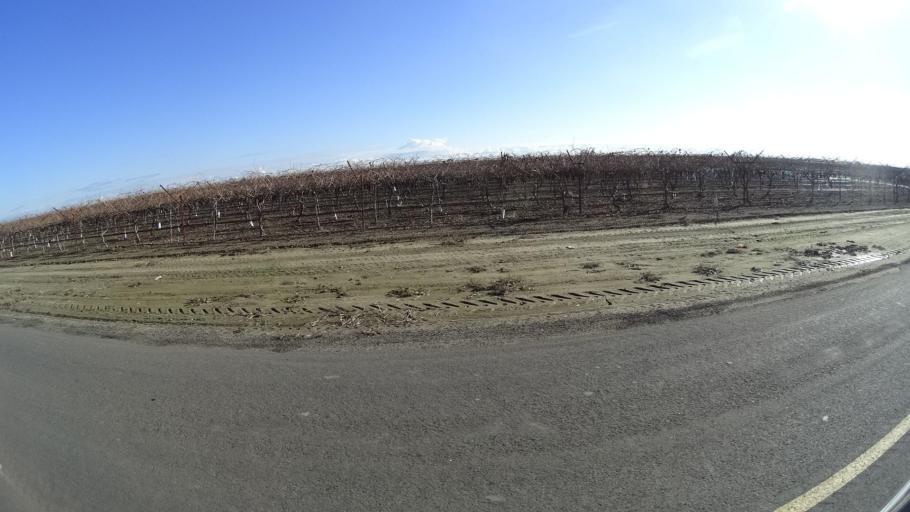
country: US
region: California
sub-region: Kern County
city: McFarland
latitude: 35.6913
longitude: -119.2764
